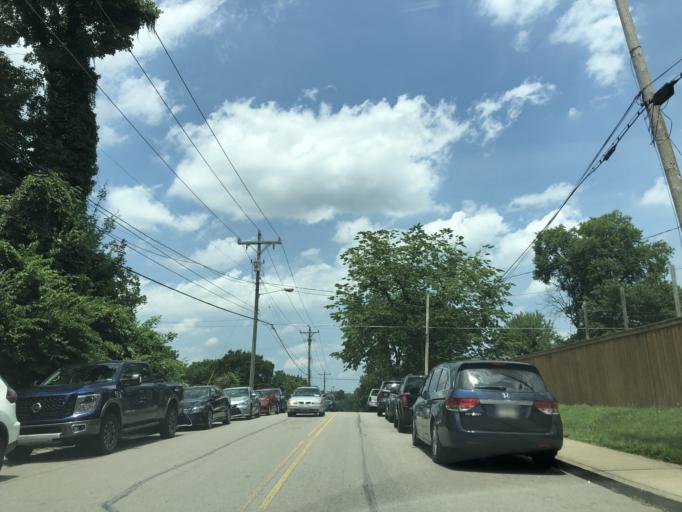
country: US
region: Tennessee
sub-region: Davidson County
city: Nashville
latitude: 36.1854
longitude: -86.7544
